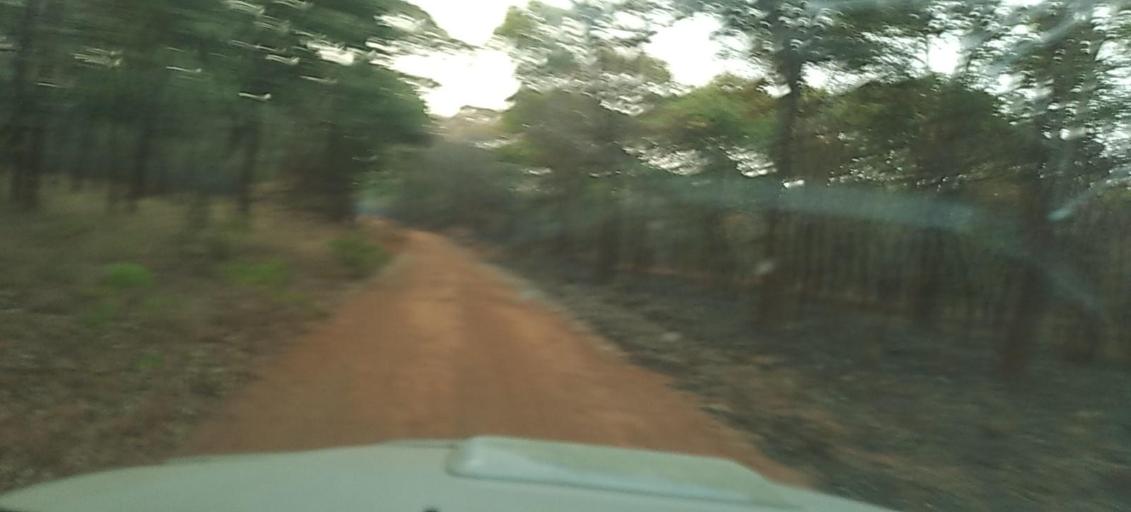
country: ZM
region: North-Western
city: Kasempa
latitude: -13.0991
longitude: 26.4032
